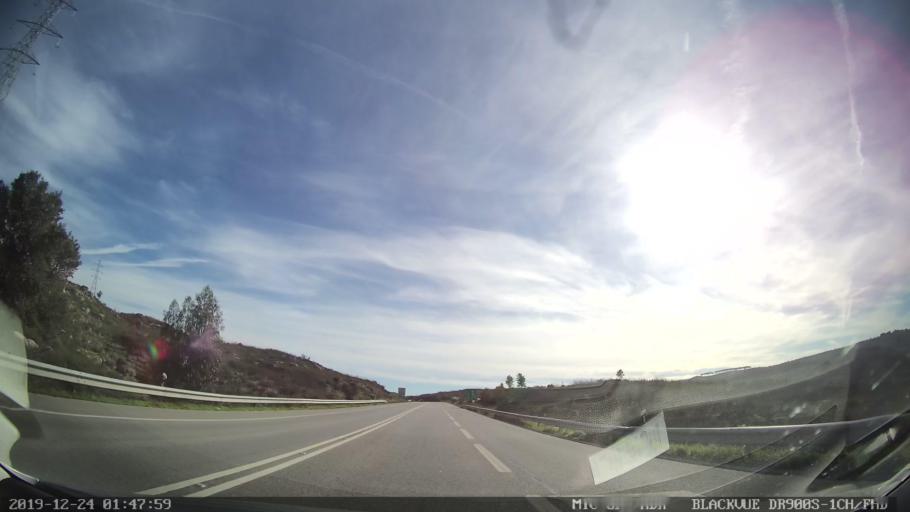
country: PT
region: Portalegre
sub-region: Nisa
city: Nisa
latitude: 39.5254
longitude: -7.7842
